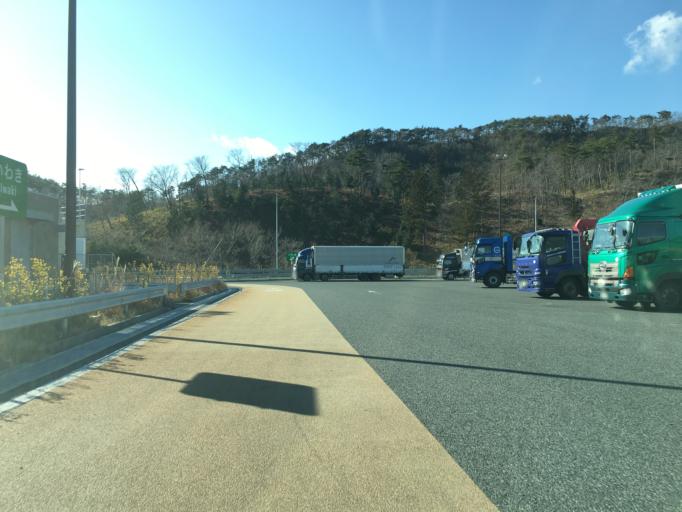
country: JP
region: Fukushima
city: Namie
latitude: 37.7137
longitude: 140.9218
